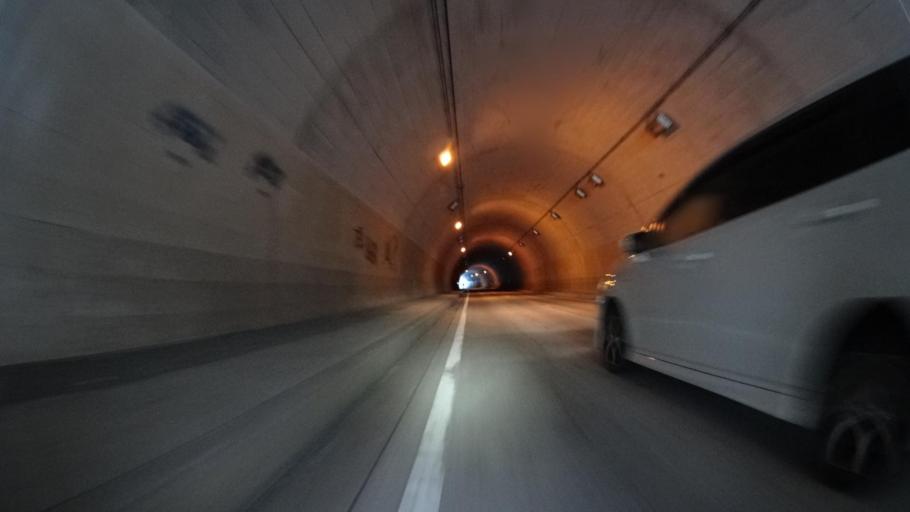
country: JP
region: Tokyo
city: Hachioji
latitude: 35.5374
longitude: 139.2512
